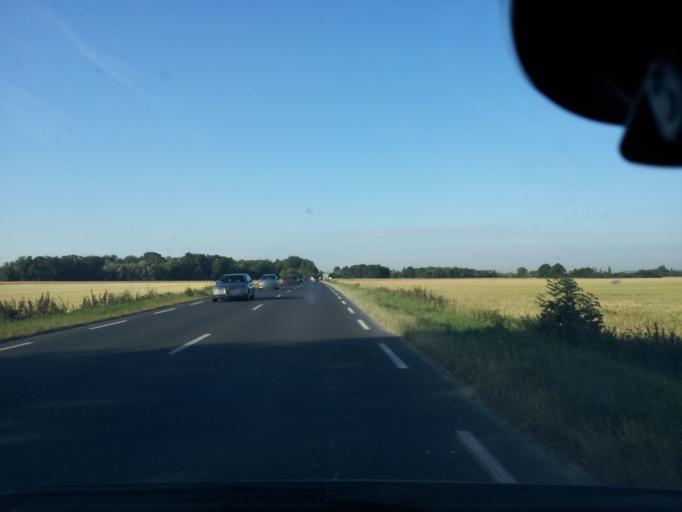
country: FR
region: Ile-de-France
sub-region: Departement de l'Essonne
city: Vert-le-Grand
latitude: 48.5907
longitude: 2.3682
